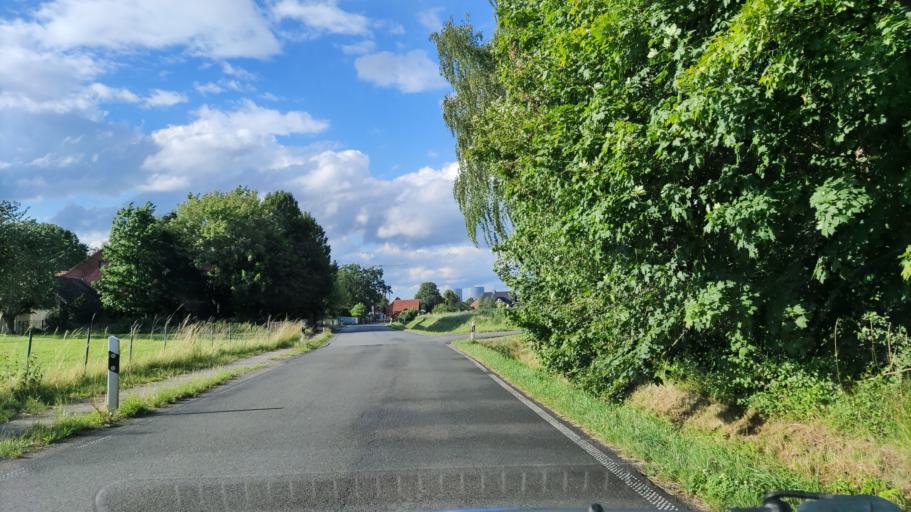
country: DE
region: North Rhine-Westphalia
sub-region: Regierungsbezirk Arnsberg
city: Welver
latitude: 51.6459
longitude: 7.9642
